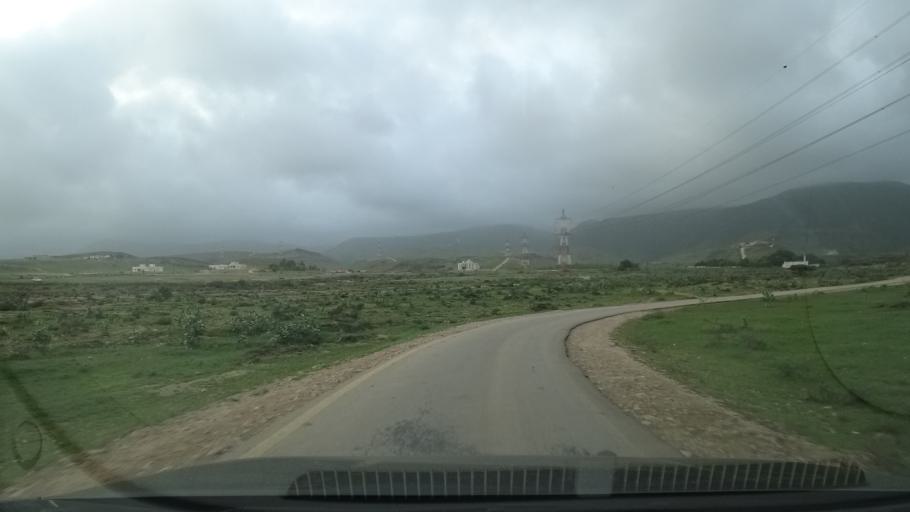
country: OM
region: Zufar
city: Salalah
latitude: 17.1159
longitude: 54.2268
